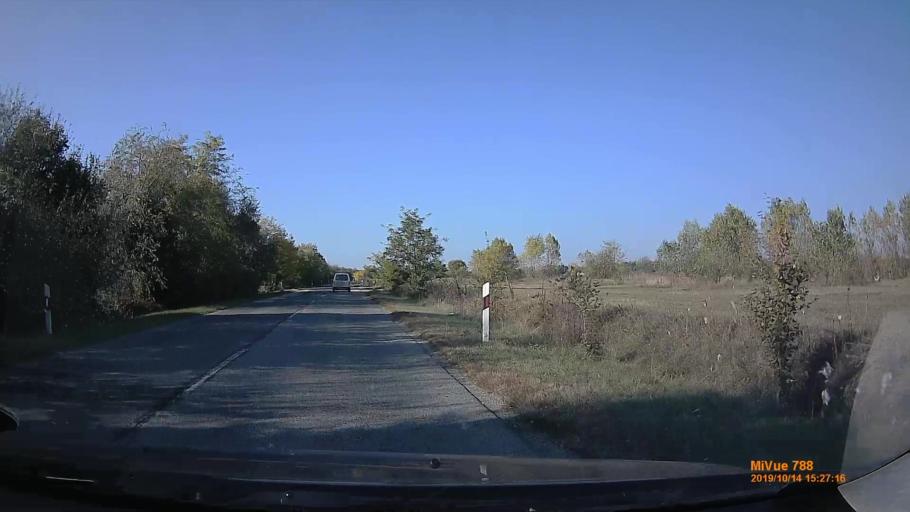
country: HU
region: Pest
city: Ecser
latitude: 47.4282
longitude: 19.3077
